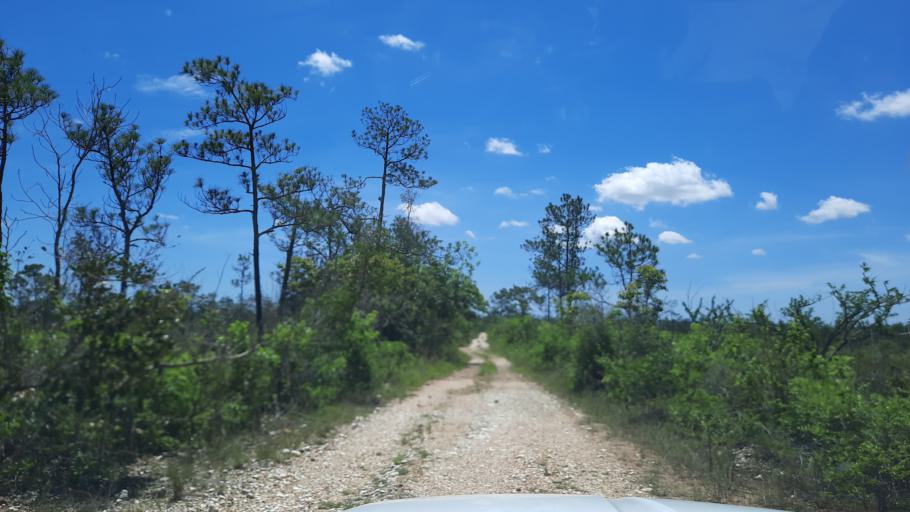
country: BZ
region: Cayo
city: Belmopan
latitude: 17.3548
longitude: -88.5487
